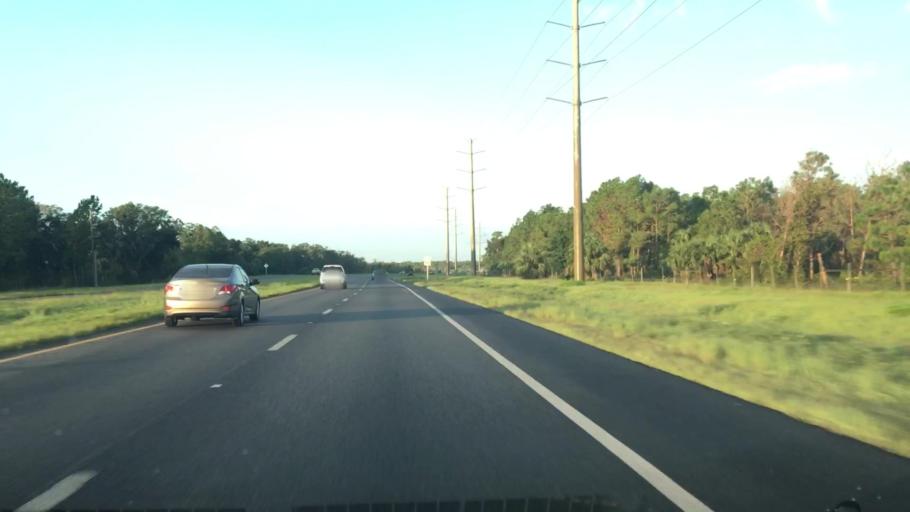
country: US
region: Florida
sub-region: Seminole County
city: Midway
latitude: 28.8196
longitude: -81.1866
